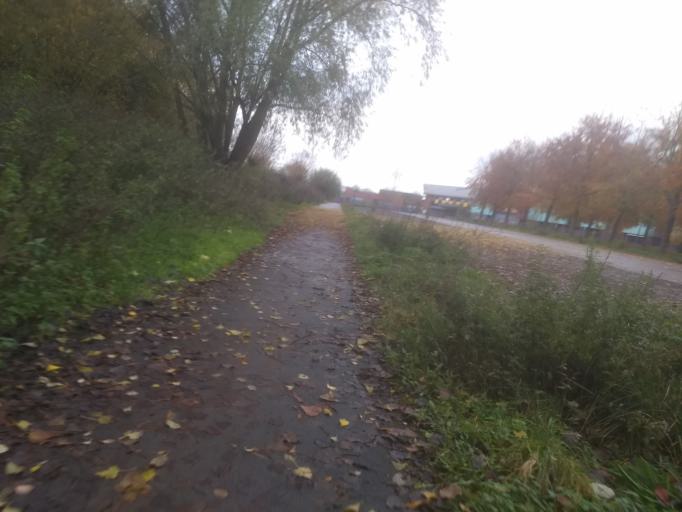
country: FR
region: Nord-Pas-de-Calais
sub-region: Departement du Pas-de-Calais
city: Achicourt
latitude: 50.2834
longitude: 2.7478
